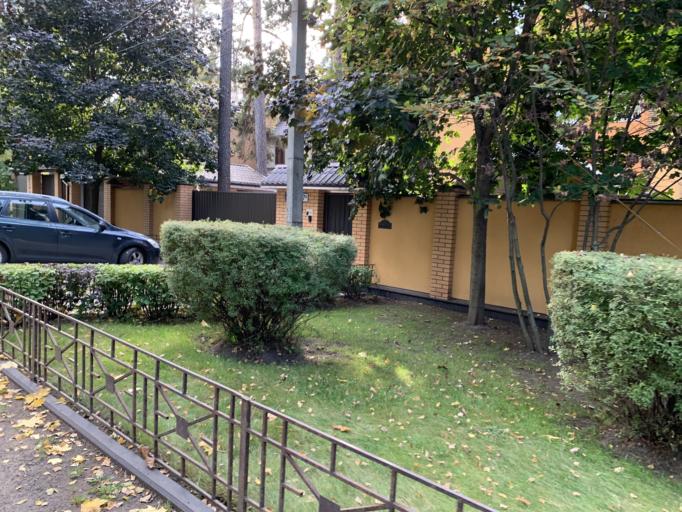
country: RU
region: Moskovskaya
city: Mamontovka
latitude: 55.9853
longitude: 37.8314
